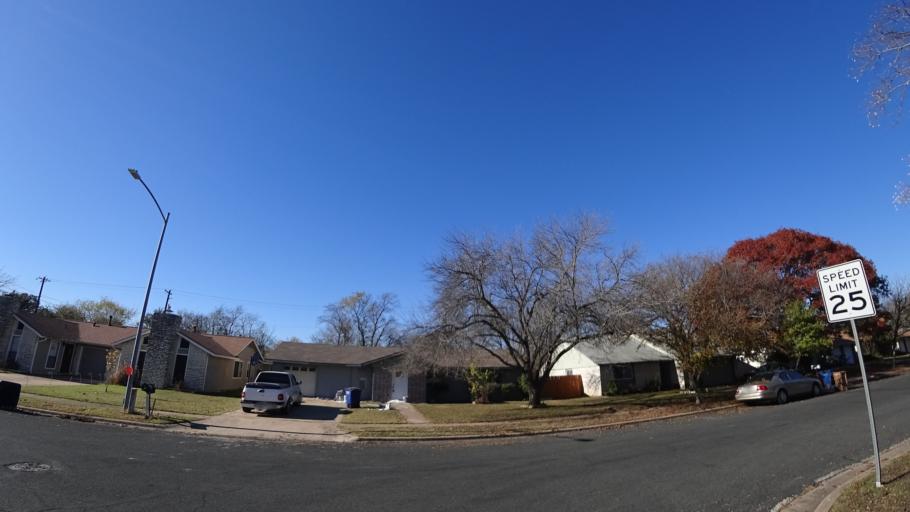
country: US
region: Texas
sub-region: Travis County
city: Wells Branch
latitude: 30.4176
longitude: -97.6978
